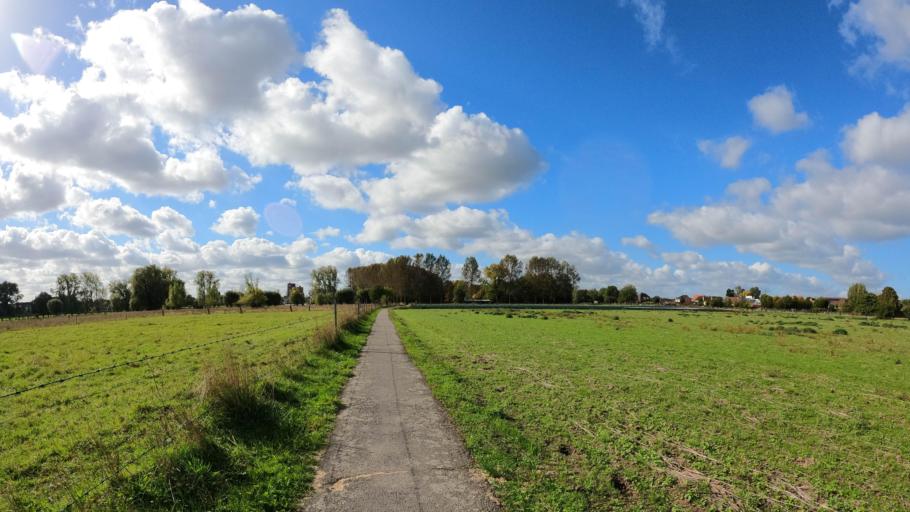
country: BE
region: Flanders
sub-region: Provincie Vlaams-Brabant
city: Merchtem
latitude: 50.9673
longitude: 4.2382
